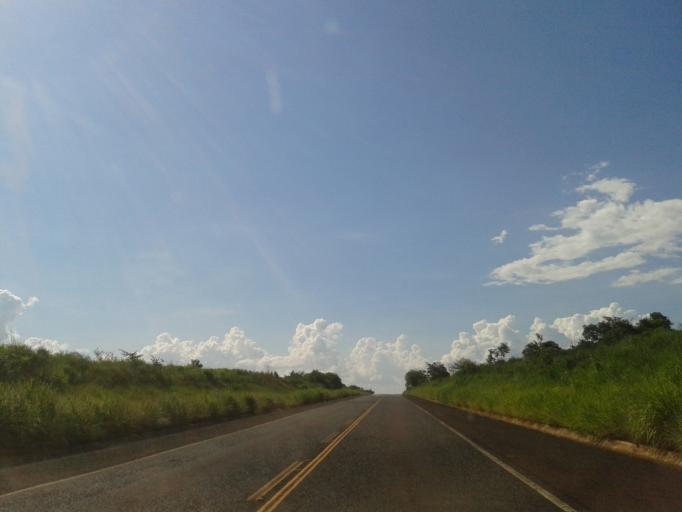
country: BR
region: Minas Gerais
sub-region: Santa Vitoria
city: Santa Vitoria
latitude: -19.0511
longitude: -50.3997
